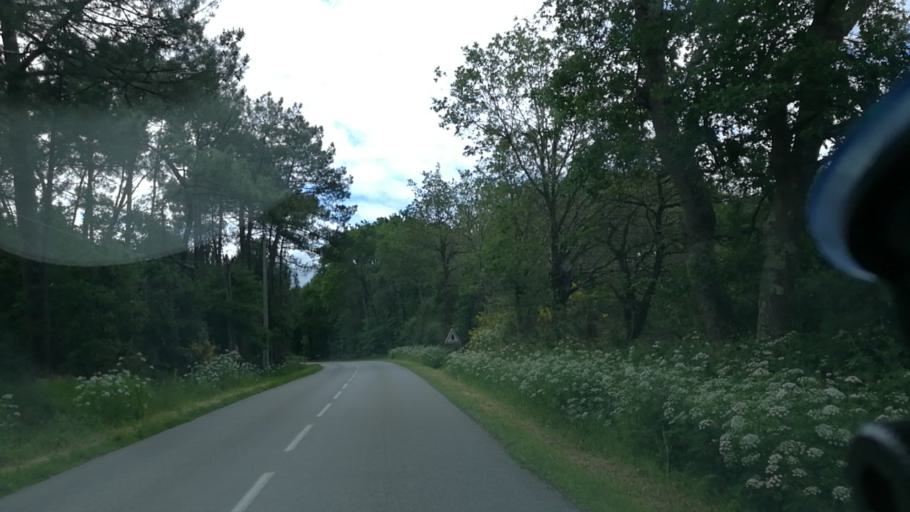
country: FR
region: Brittany
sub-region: Departement du Morbihan
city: Penestin
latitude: 47.4763
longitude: -2.4340
